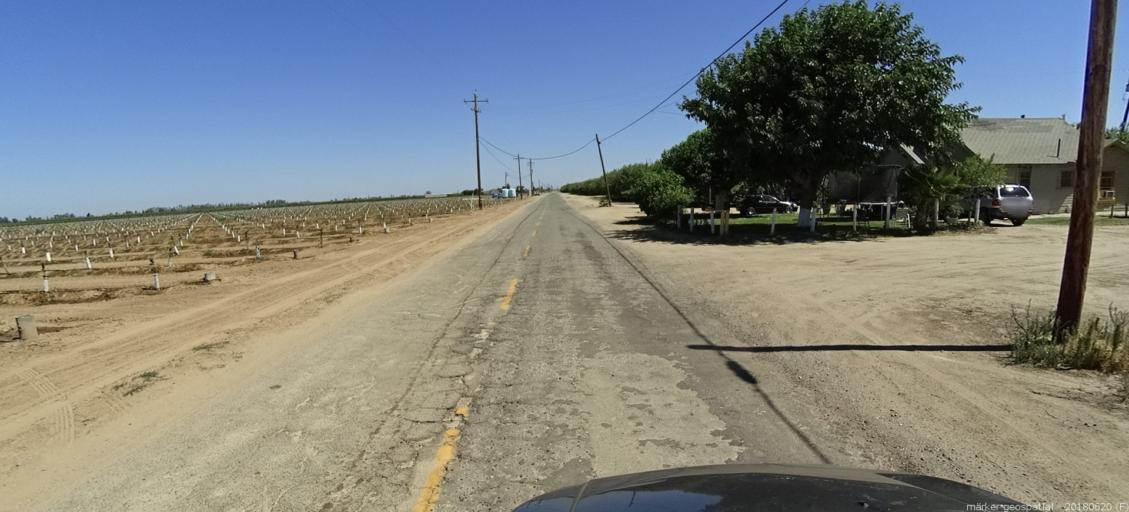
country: US
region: California
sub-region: Madera County
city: Parkwood
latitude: 36.8920
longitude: -120.0105
